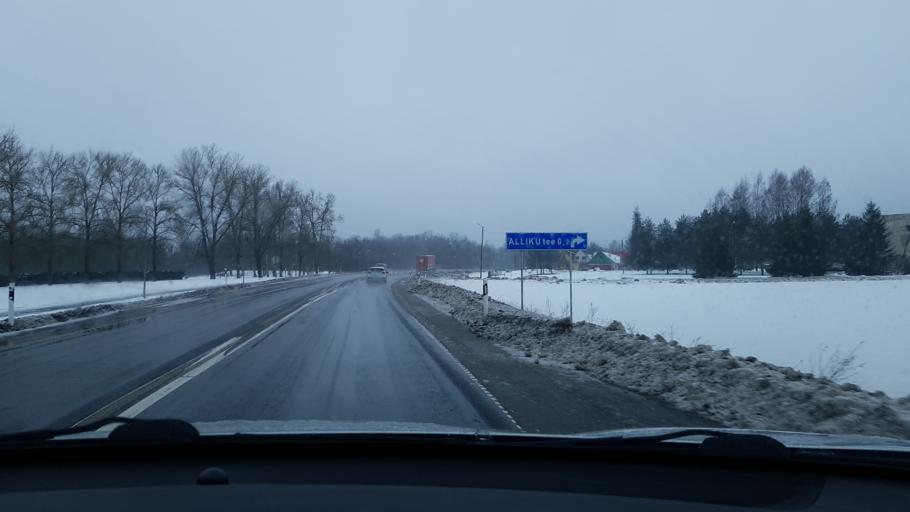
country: EE
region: Jaervamaa
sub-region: Tueri vald
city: Tueri
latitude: 58.8272
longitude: 25.4580
